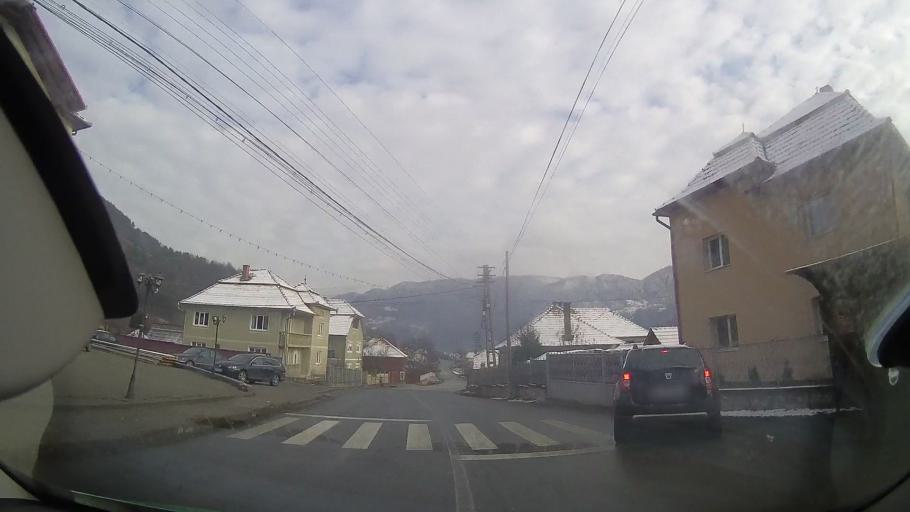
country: RO
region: Alba
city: Salciua de Sus
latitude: 46.3984
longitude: 23.4194
